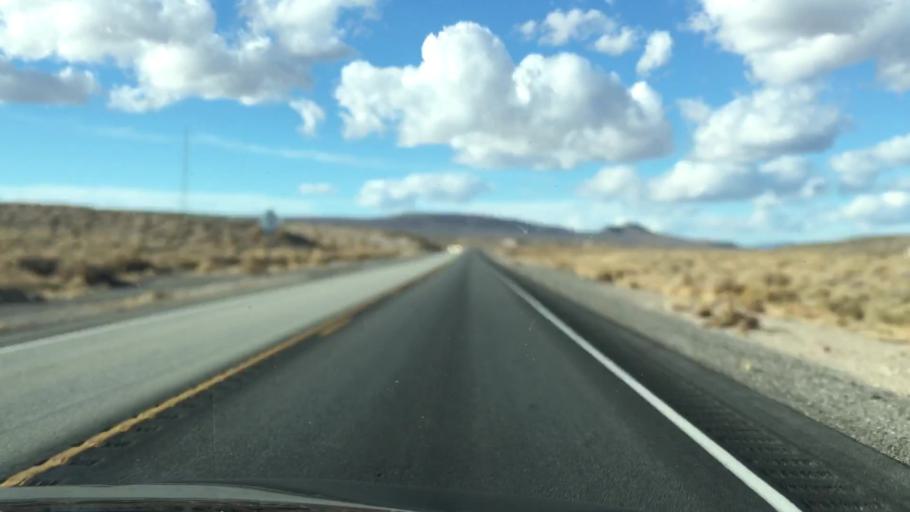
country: US
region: Nevada
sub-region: Nye County
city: Beatty
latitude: 37.0368
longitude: -116.7624
